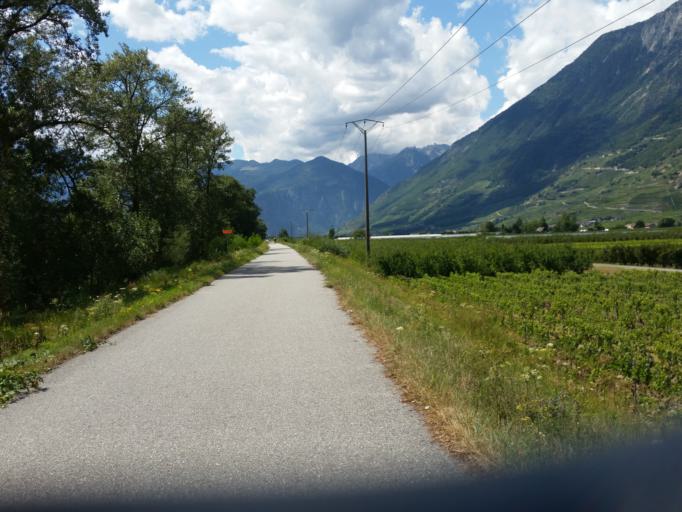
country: CH
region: Valais
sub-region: Martigny District
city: Saxon
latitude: 46.1549
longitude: 7.1633
